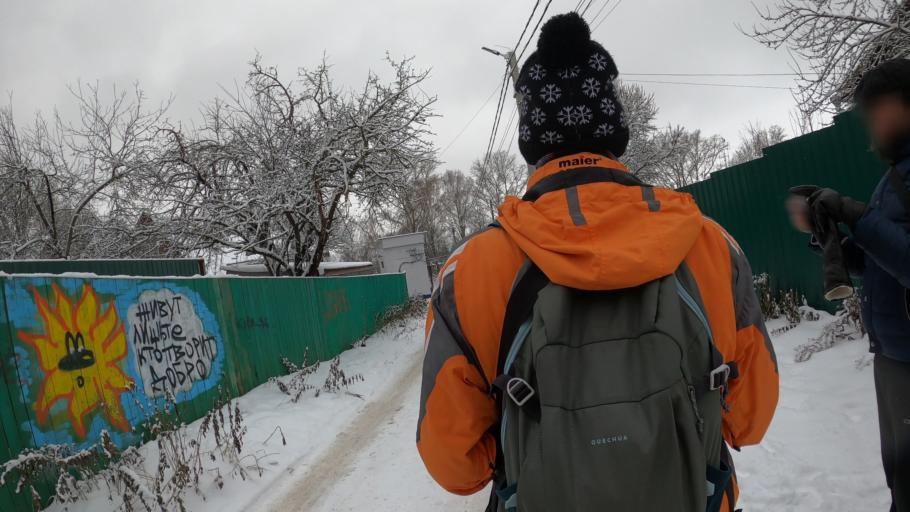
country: RU
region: Jaroslavl
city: Pereslavl'-Zalesskiy
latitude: 56.7450
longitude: 38.8627
